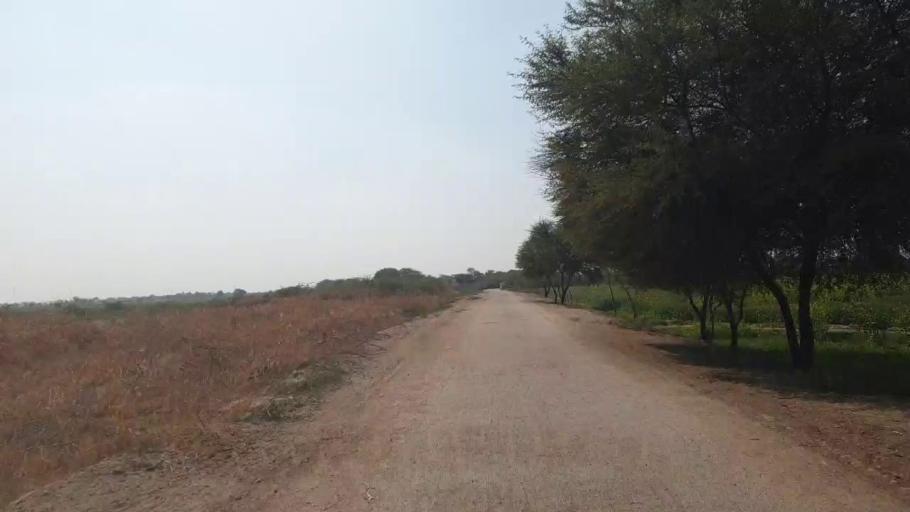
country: PK
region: Sindh
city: Chambar
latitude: 25.3855
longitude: 68.9228
